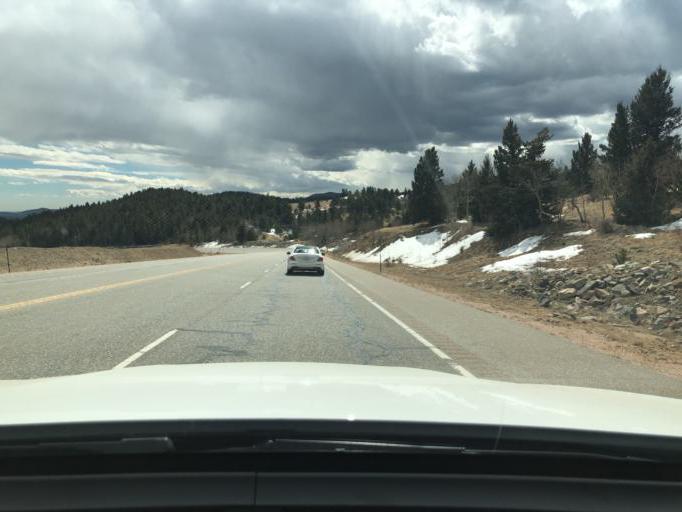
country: US
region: Colorado
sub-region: Gilpin County
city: Central City
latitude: 39.7872
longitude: -105.4967
